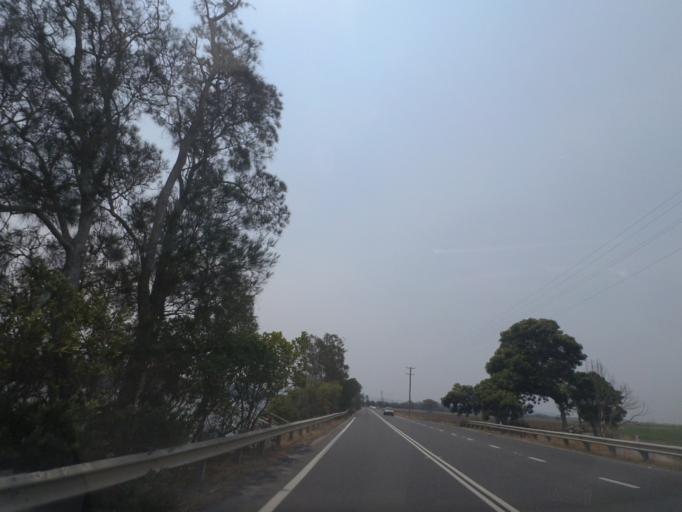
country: AU
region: New South Wales
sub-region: Richmond Valley
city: Evans Head
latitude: -28.9774
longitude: 153.4619
